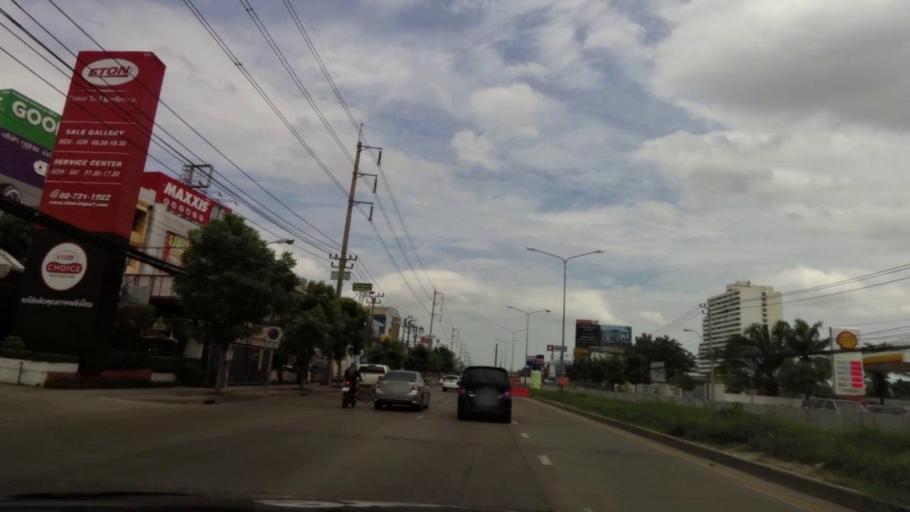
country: TH
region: Bangkok
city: Suan Luang
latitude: 13.7037
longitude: 100.6459
